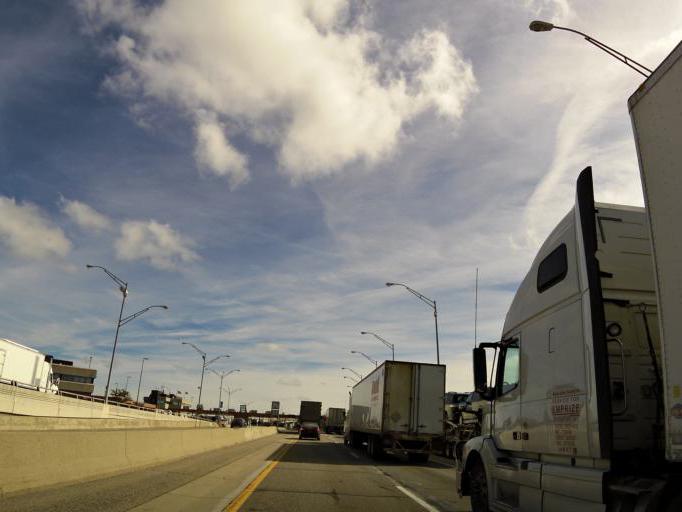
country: US
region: Michigan
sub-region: Saint Clair County
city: Port Huron
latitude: 42.9979
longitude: -82.4384
